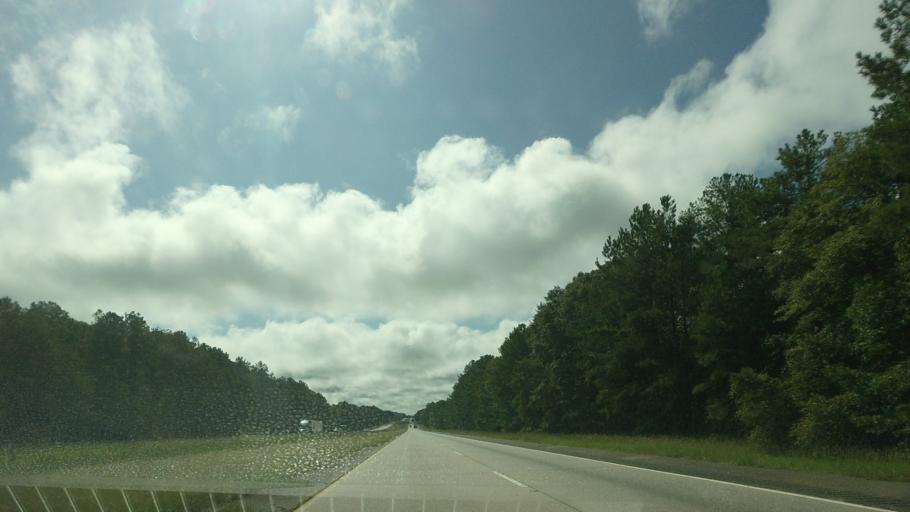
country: US
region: Georgia
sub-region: Houston County
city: Robins Air Force Base
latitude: 32.6987
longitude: -83.5060
